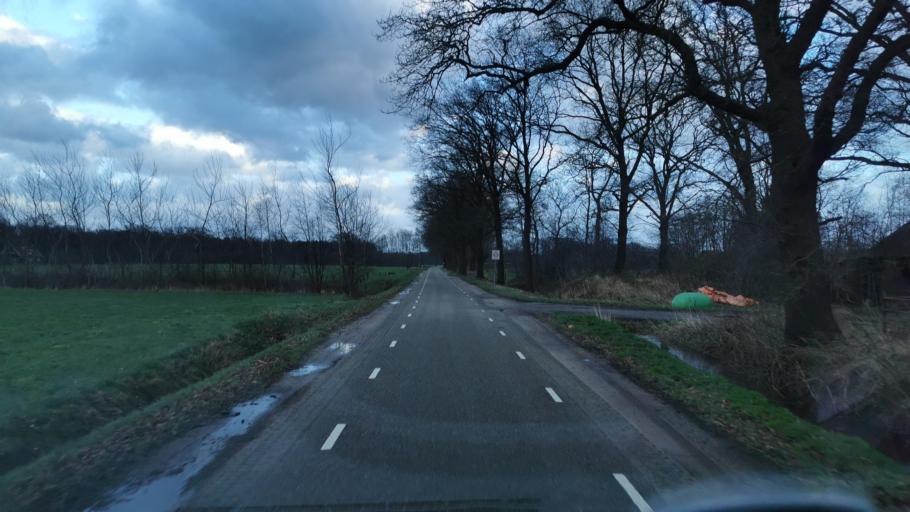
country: DE
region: Lower Saxony
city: Nordhorn
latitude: 52.4147
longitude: 7.0190
